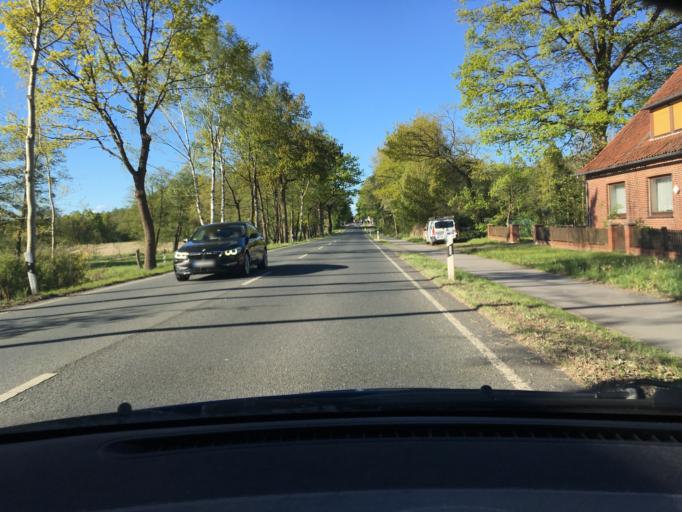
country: DE
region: Lower Saxony
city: Schneverdingen
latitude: 53.0688
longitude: 9.8615
